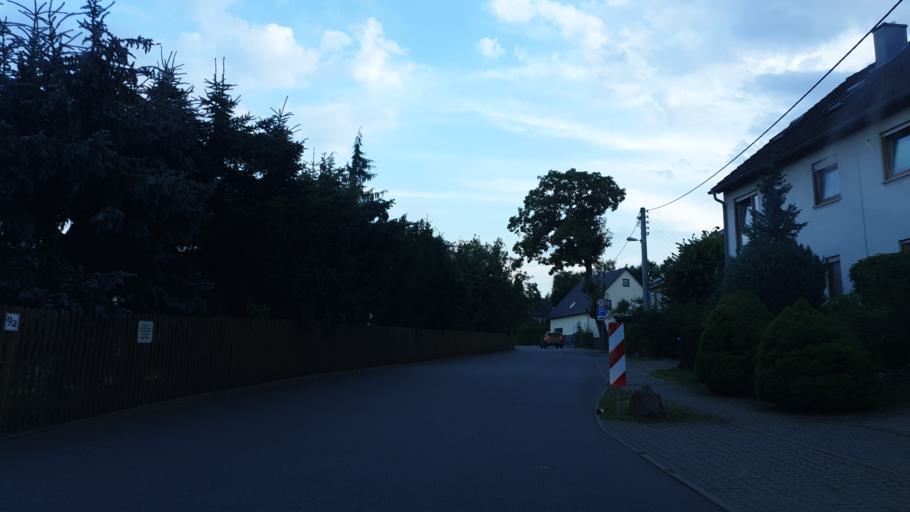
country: DE
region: Saxony
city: Kirchberg
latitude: 50.7925
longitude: 12.7859
